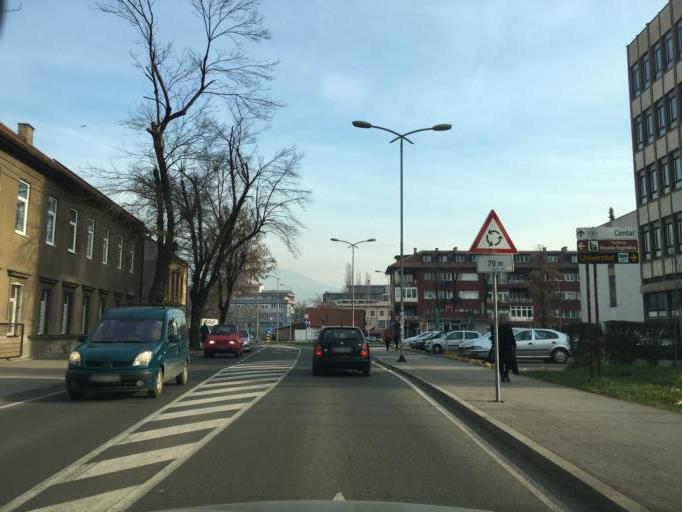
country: BA
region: Federation of Bosnia and Herzegovina
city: Zenica
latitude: 44.2007
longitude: 17.9015
